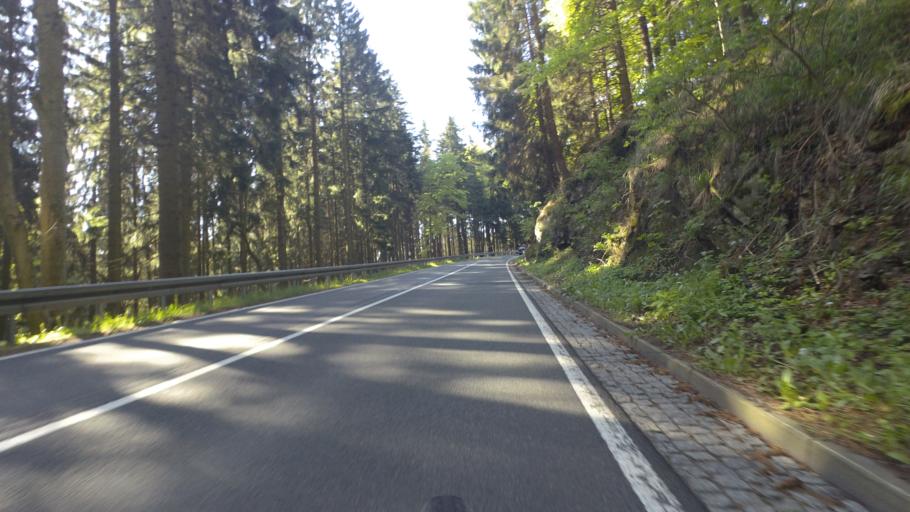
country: DE
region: Saxony-Anhalt
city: Benneckenstein
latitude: 51.7588
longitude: 10.6993
